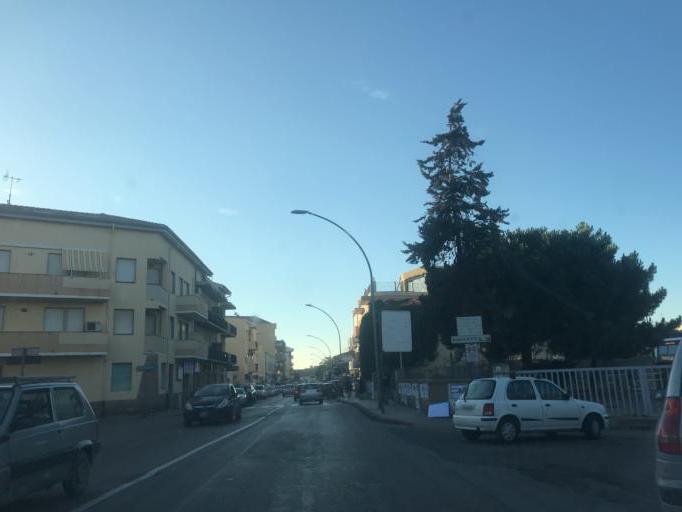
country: IT
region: Sardinia
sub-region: Provincia di Sassari
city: Alghero
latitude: 40.5741
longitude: 8.3220
